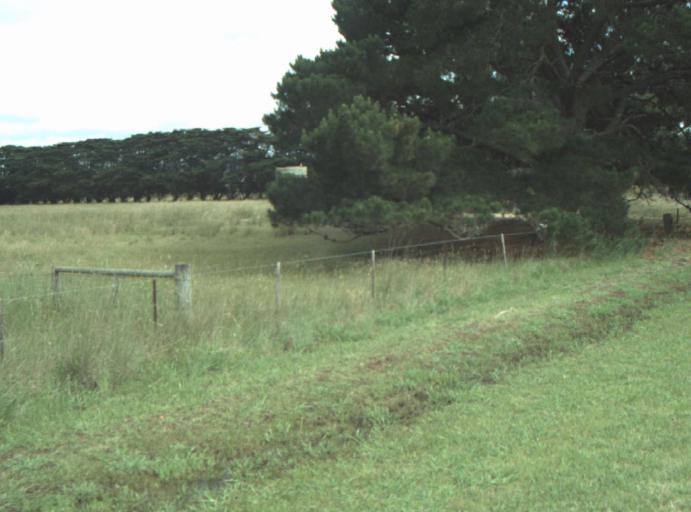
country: AU
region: Victoria
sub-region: Greater Geelong
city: Lara
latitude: -37.8650
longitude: 144.3510
